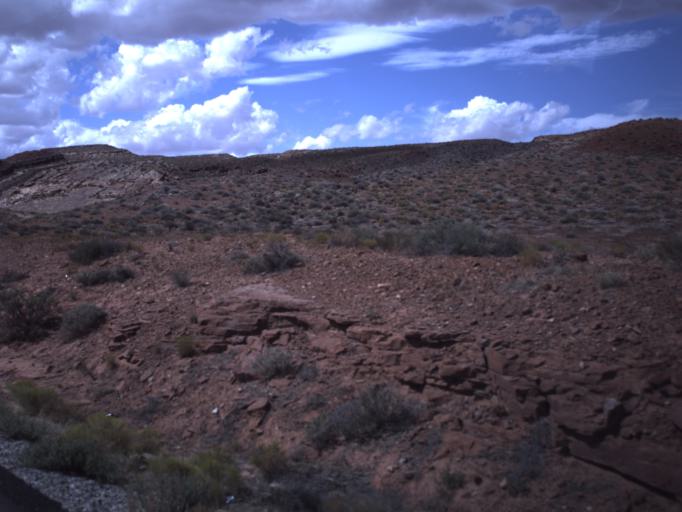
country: US
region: Arizona
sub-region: Navajo County
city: Kayenta
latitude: 37.1305
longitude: -109.8931
